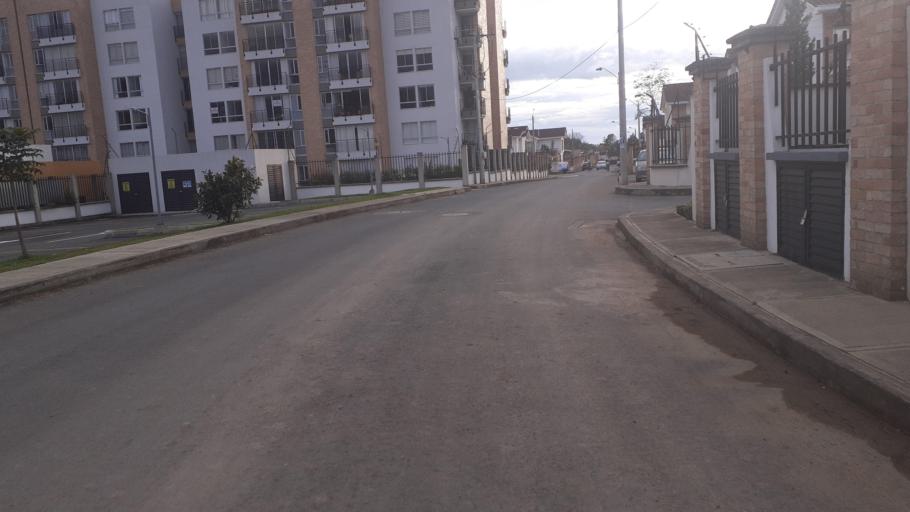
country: CO
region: Cauca
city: Popayan
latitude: 2.4632
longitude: -76.5833
